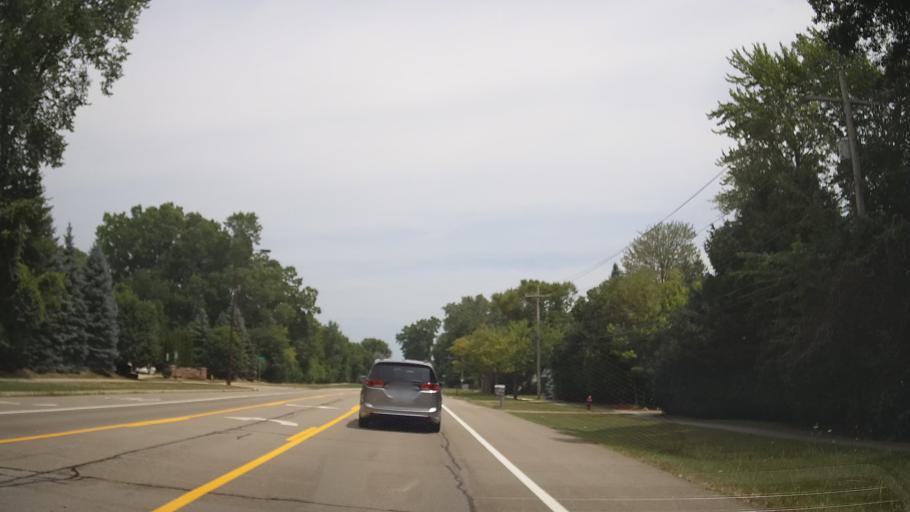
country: US
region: Michigan
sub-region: Oakland County
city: Troy
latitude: 42.6075
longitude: -83.1070
